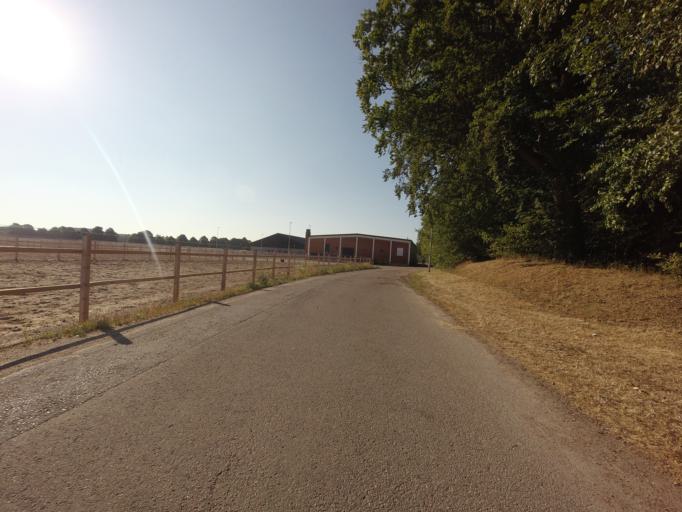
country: SE
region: Skane
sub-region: Landskrona
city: Landskrona
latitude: 55.8945
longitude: 12.8357
